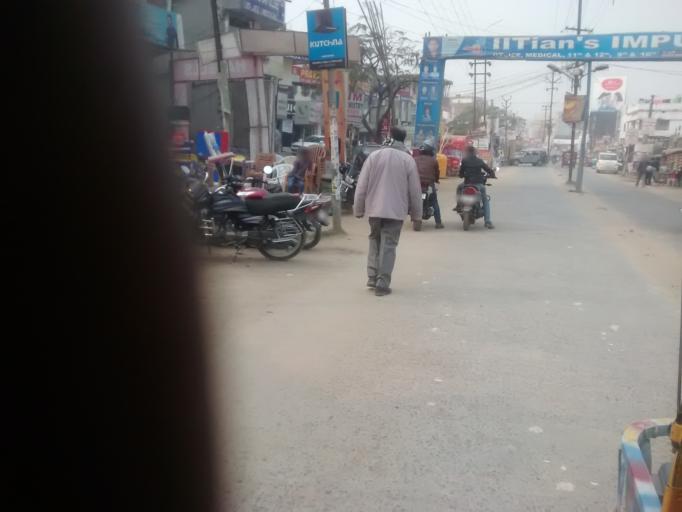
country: IN
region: Bihar
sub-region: Muzaffarpur
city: Muzaffarpur
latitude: 26.1052
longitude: 85.3985
